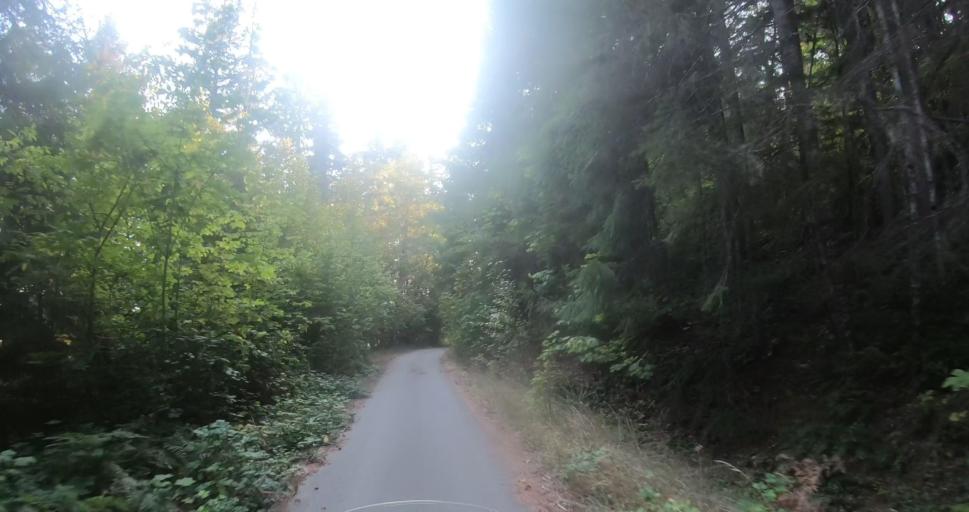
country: US
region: Washington
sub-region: Lewis County
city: Morton
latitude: 46.5438
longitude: -121.9100
